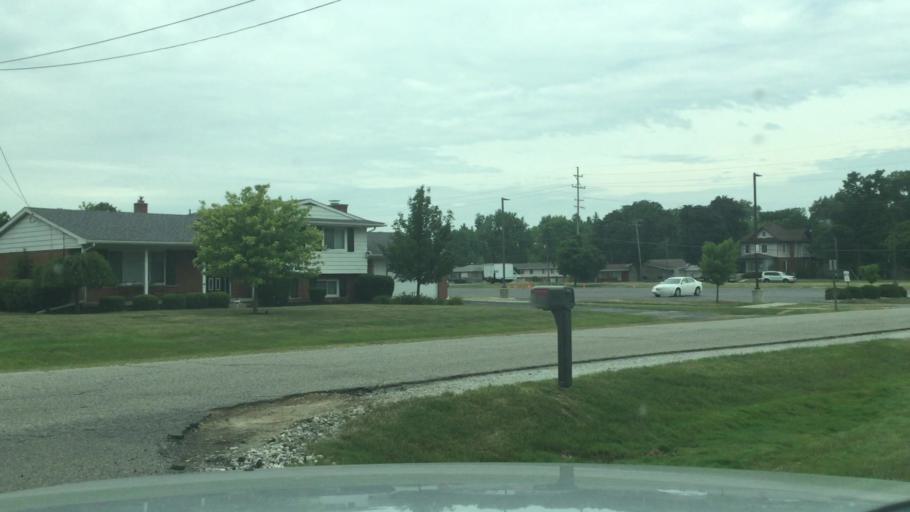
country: US
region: Michigan
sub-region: Genesee County
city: Flint
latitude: 42.9727
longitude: -83.7028
